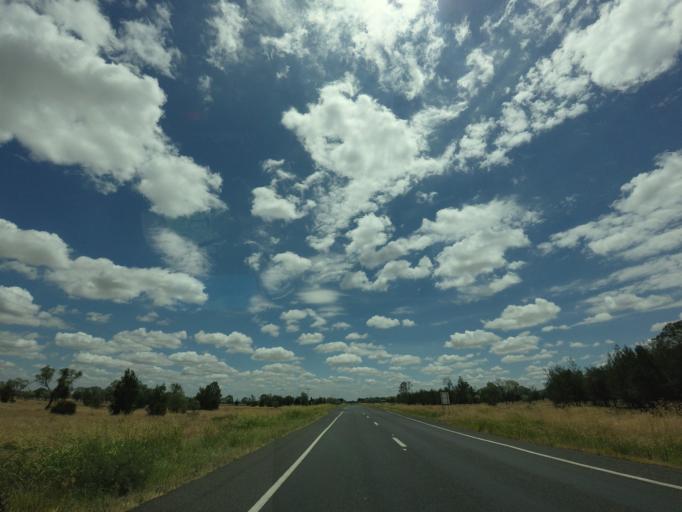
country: AU
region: New South Wales
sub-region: Moree Plains
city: Boggabilla
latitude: -28.9116
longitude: 150.1321
